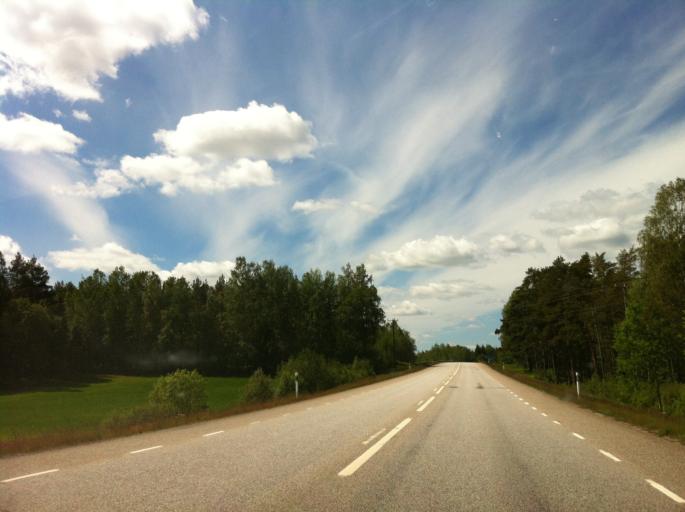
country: SE
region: Vaestra Goetaland
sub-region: Amals Kommun
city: Amal
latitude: 58.9893
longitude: 12.6681
